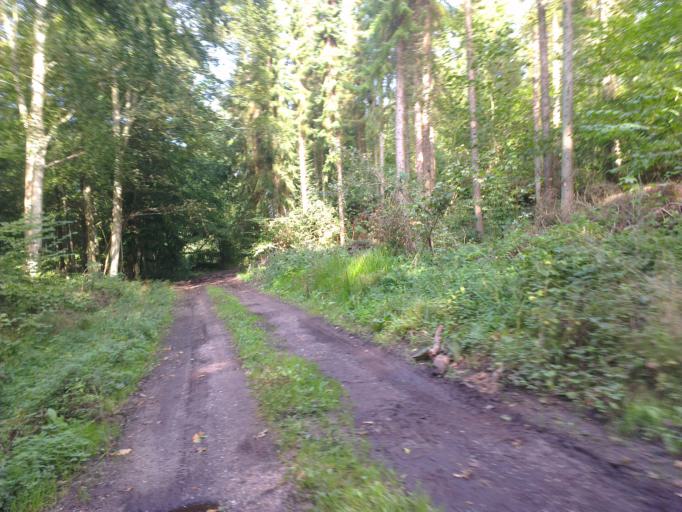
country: DK
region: Capital Region
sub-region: Frederikssund Kommune
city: Jaegerspris
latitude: 55.8893
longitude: 11.9654
